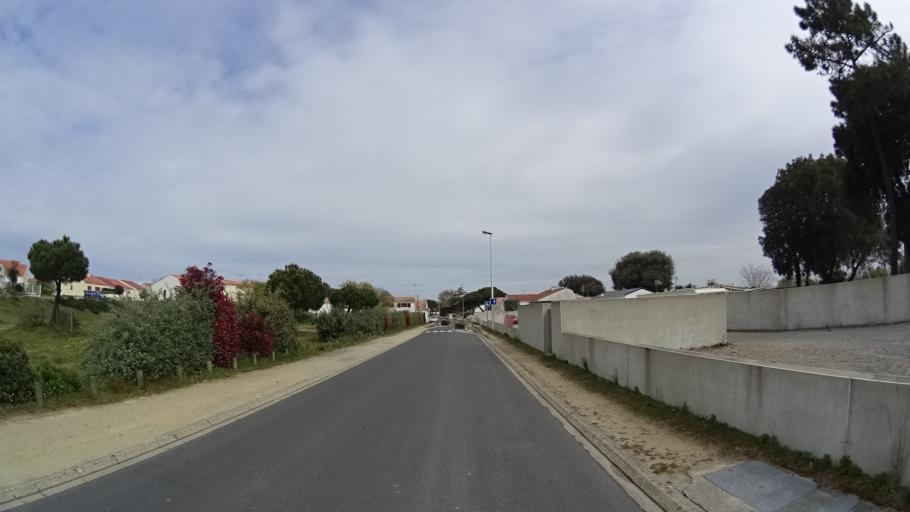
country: FR
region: Pays de la Loire
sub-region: Departement de la Vendee
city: La Barre-de-Monts
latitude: 46.8872
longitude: -2.1221
